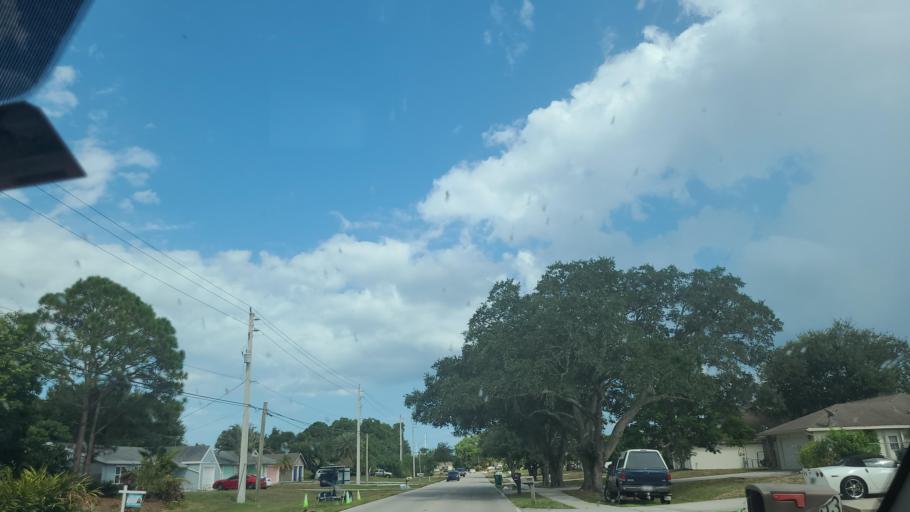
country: US
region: Florida
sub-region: Saint Lucie County
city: Port Saint Lucie
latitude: 27.2563
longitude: -80.3665
